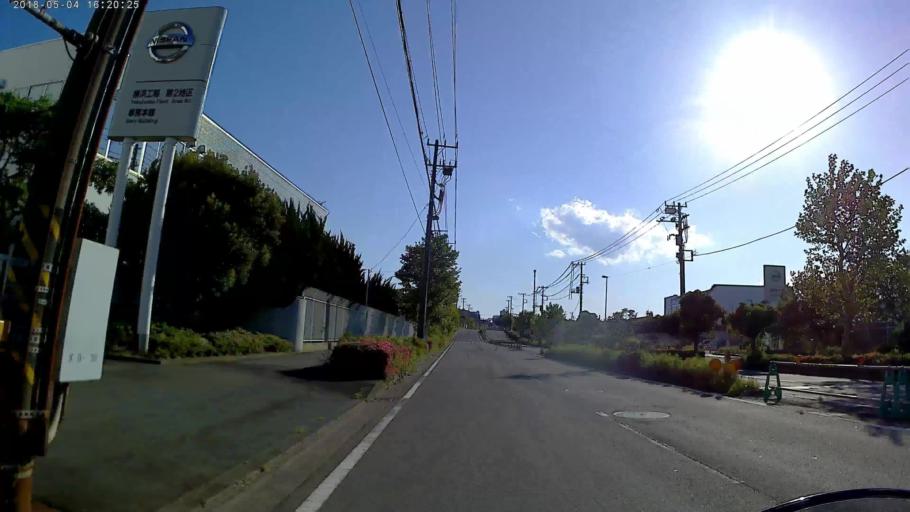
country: JP
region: Kanagawa
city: Yokohama
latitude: 35.4814
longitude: 139.6626
